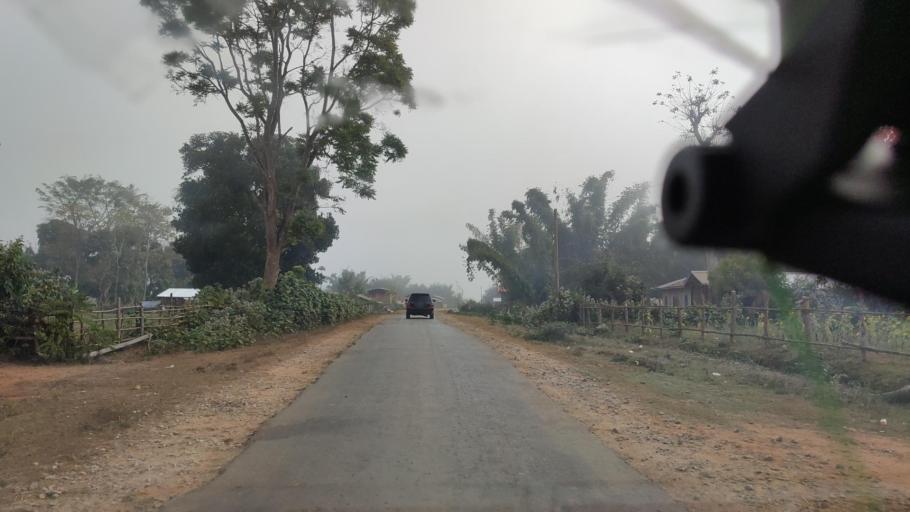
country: MM
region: Shan
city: Taunggyi
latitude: 21.2975
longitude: 97.7516
